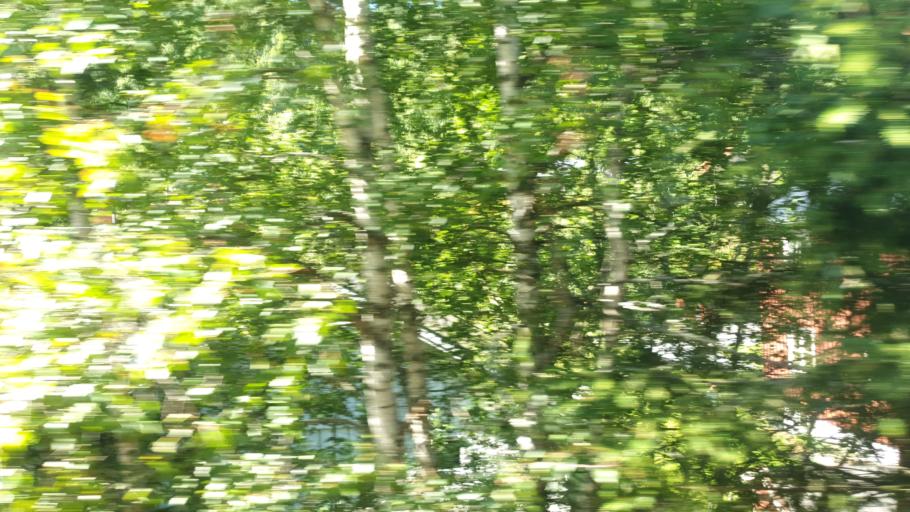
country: NO
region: Sor-Trondelag
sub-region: Meldal
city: Meldal
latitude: 63.1281
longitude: 9.7063
